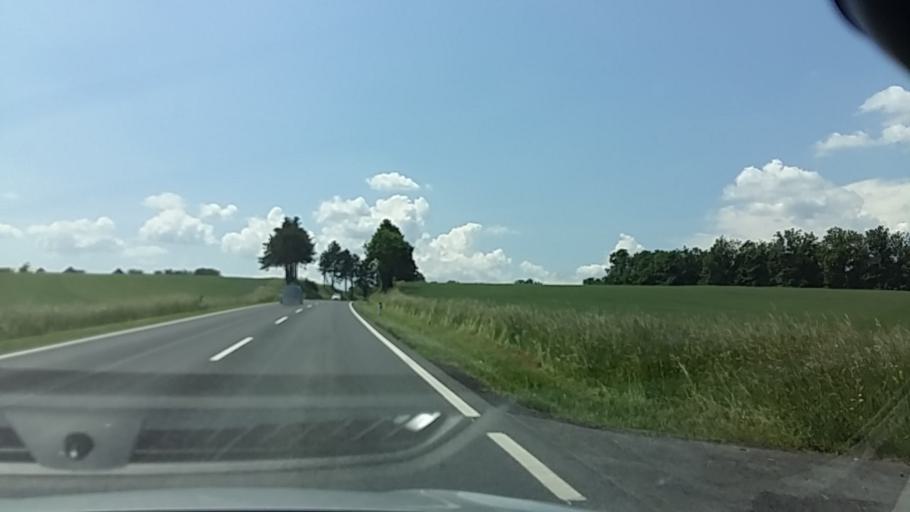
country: AT
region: Burgenland
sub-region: Politischer Bezirk Oberpullendorf
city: Piringsdorf
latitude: 47.4329
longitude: 16.4039
